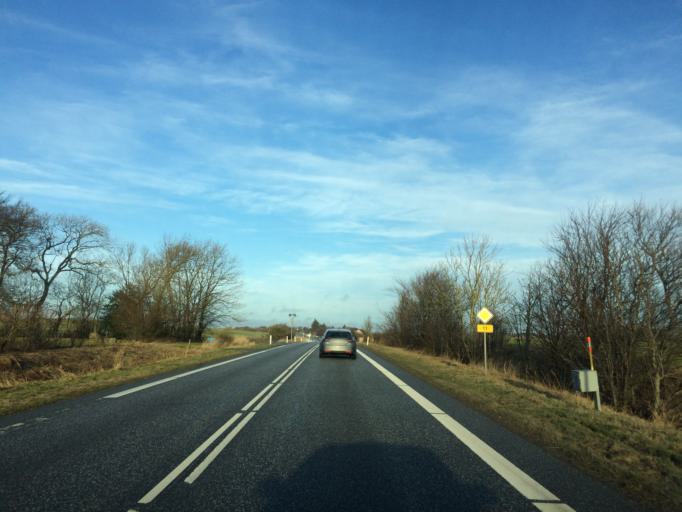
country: DK
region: North Denmark
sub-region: Thisted Kommune
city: Hurup
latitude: 56.7945
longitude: 8.4701
